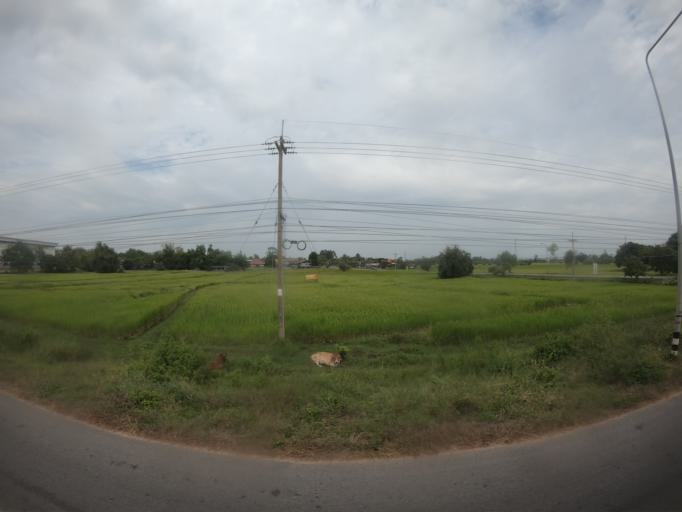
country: TH
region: Roi Et
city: Changhan
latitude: 16.0946
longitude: 103.5400
